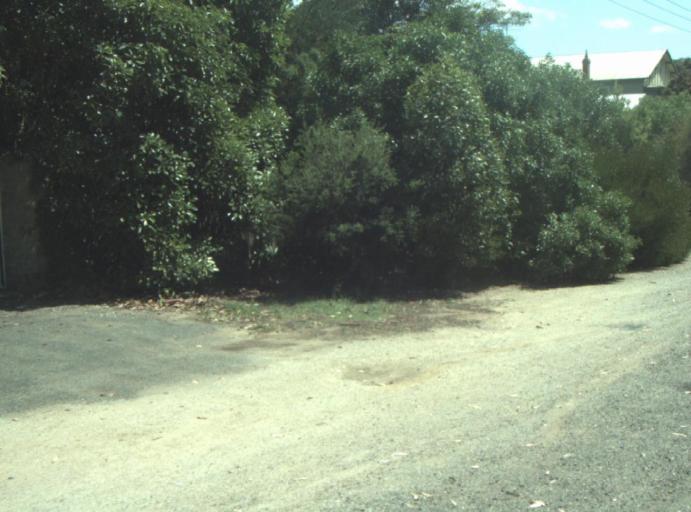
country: AU
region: Victoria
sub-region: Greater Geelong
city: Leopold
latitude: -38.2875
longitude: 144.4976
